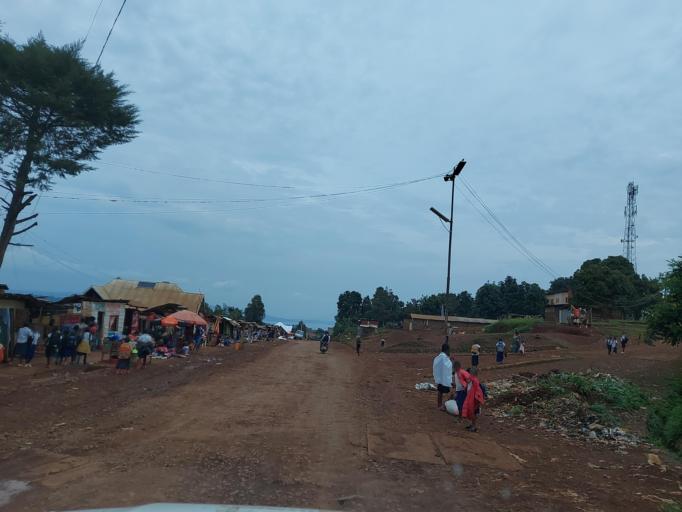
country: CD
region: South Kivu
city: Bukavu
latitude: -2.4810
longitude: 28.8210
